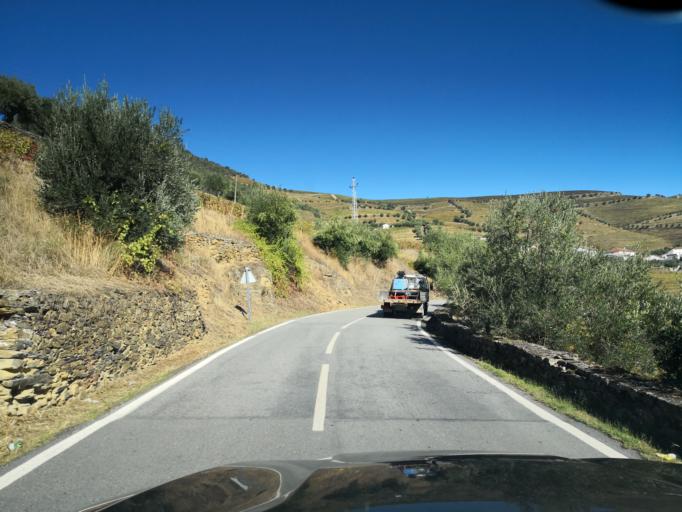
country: PT
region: Viseu
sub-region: Tabuaco
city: Tabuaco
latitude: 41.1695
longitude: -7.5446
